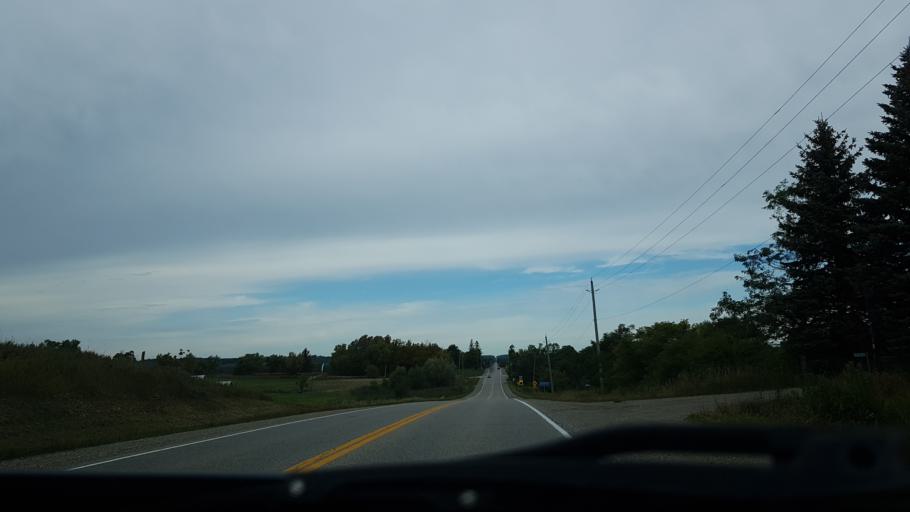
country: CA
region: Ontario
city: Shelburne
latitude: 44.1391
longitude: -80.0309
